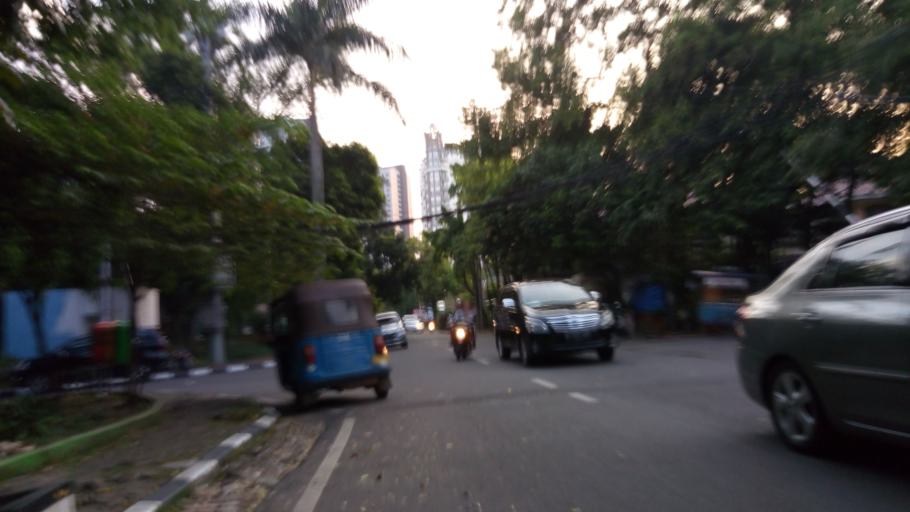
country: ID
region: Jakarta Raya
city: Jakarta
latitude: -6.2443
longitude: 106.7906
